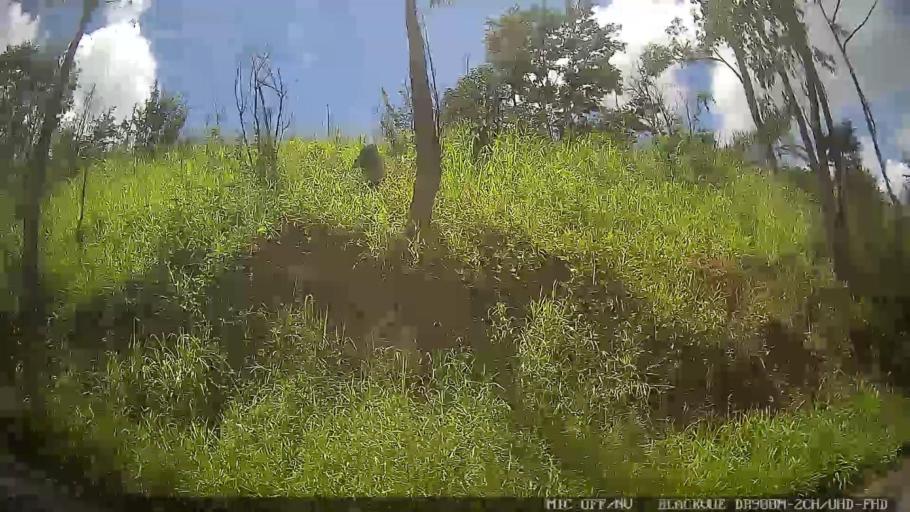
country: BR
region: Sao Paulo
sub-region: Amparo
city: Amparo
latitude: -22.7849
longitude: -46.7150
